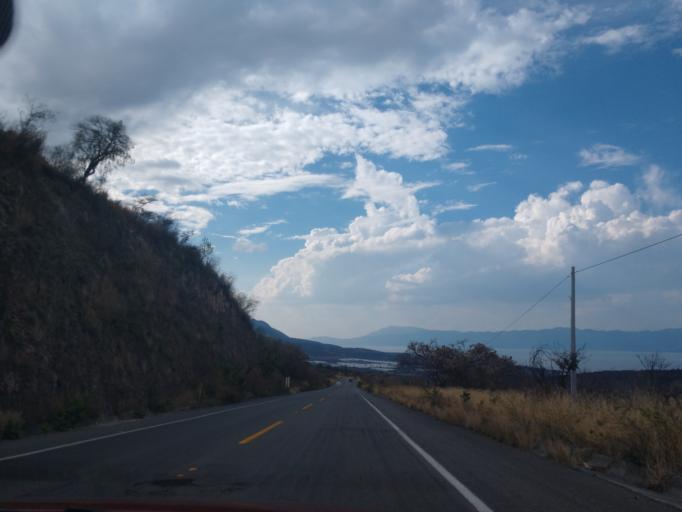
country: MX
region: Jalisco
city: Tizapan el Alto
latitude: 20.1265
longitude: -103.1605
